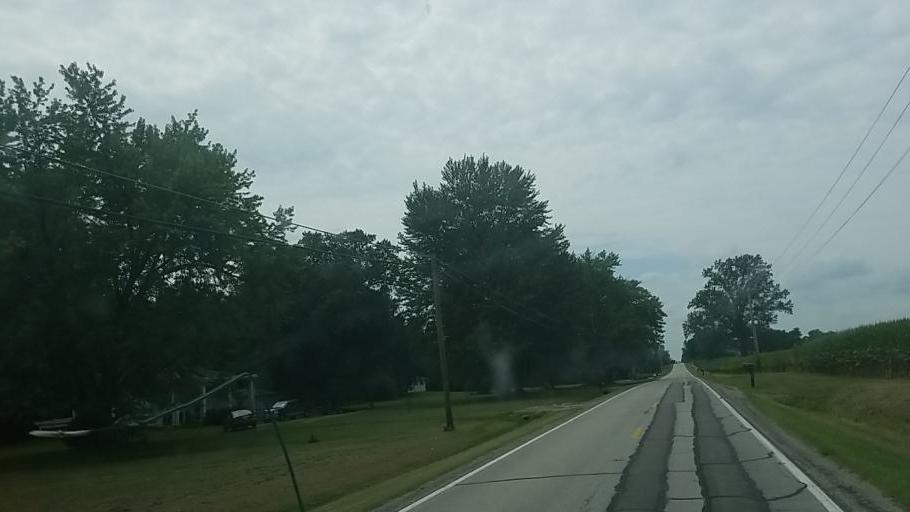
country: US
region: Ohio
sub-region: Franklin County
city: Groveport
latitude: 39.8272
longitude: -82.8768
